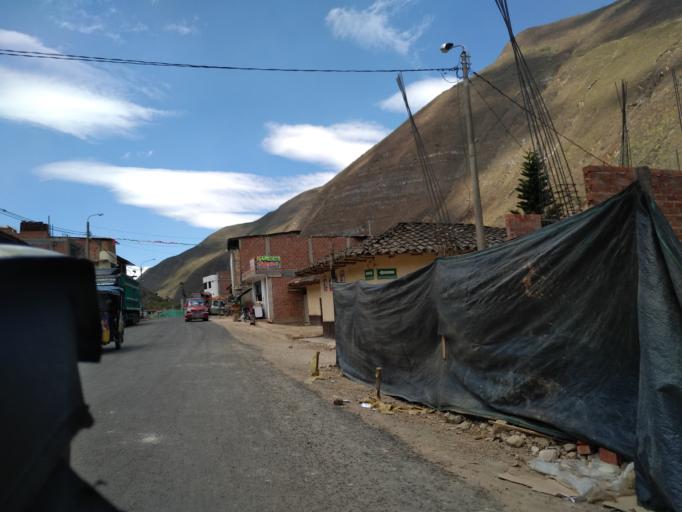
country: PE
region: Amazonas
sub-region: Provincia de Chachapoyas
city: Duraznopampa
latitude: -6.5660
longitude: -77.8292
